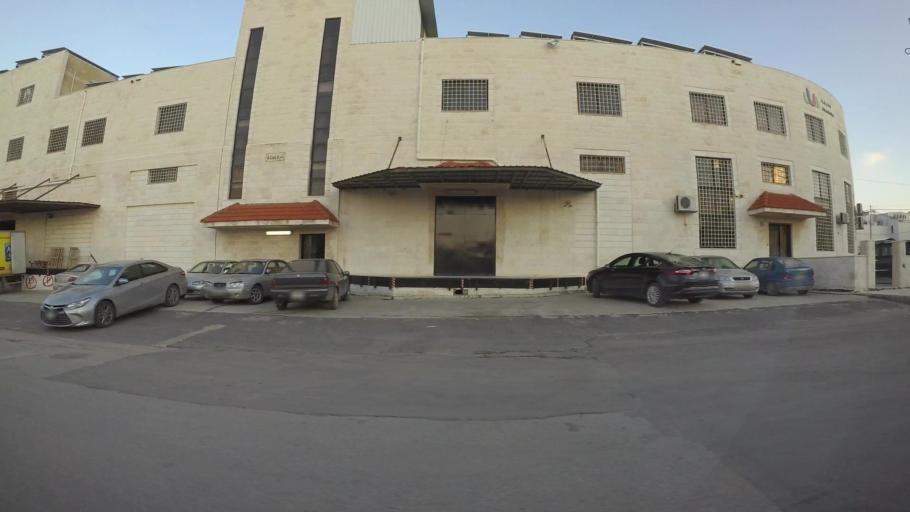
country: JO
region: Amman
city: Al Bunayyat ash Shamaliyah
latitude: 31.9086
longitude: 35.9183
